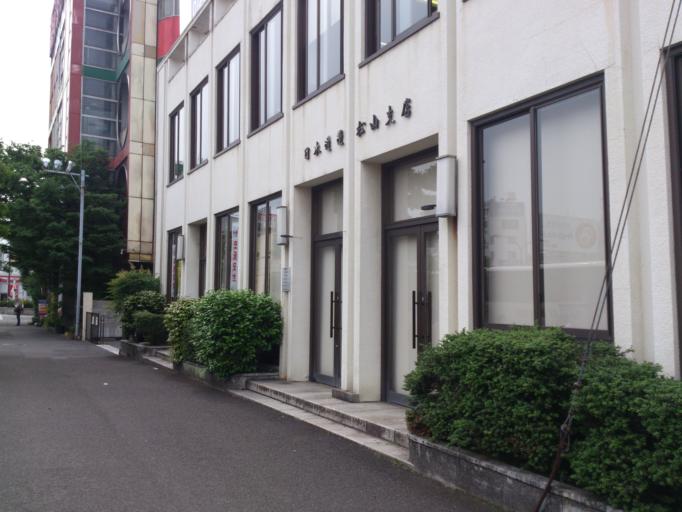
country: JP
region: Ehime
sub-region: Shikoku-chuo Shi
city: Matsuyama
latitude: 33.8397
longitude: 132.7516
